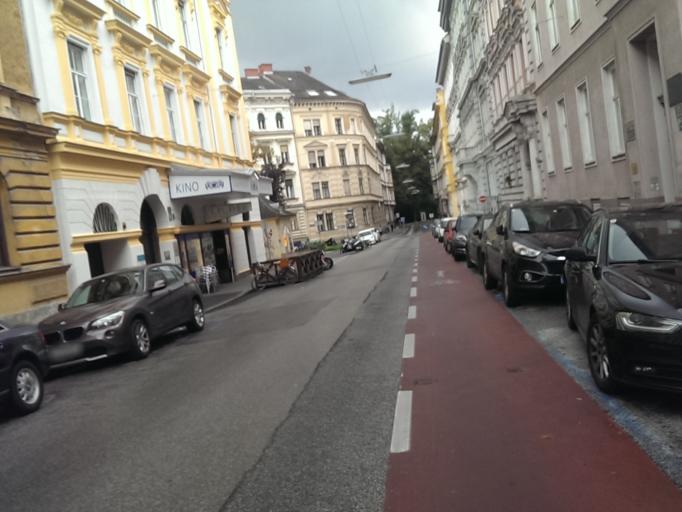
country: AT
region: Styria
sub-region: Graz Stadt
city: Graz
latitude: 47.0699
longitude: 15.4496
